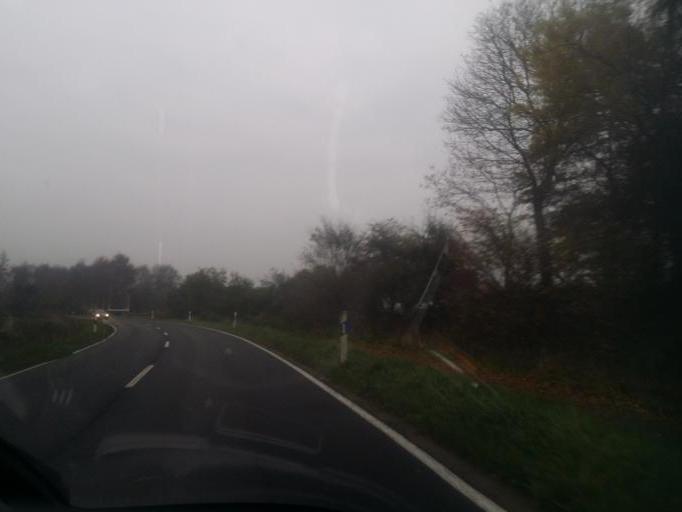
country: DE
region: Schleswig-Holstein
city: Grosssolt
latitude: 54.6961
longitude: 9.5148
